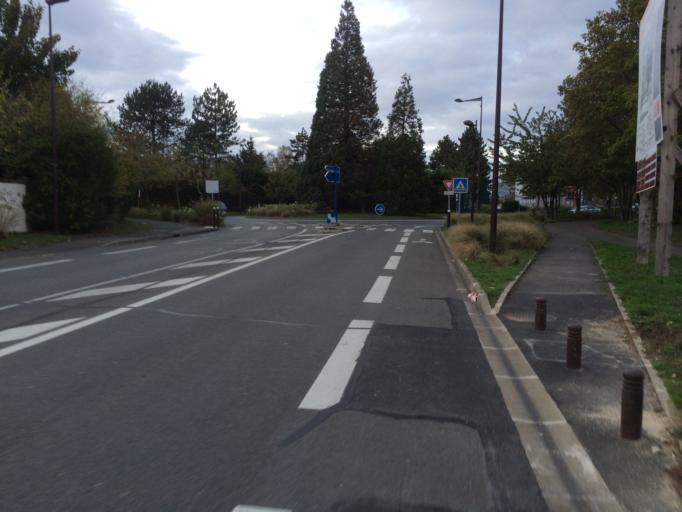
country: FR
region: Ile-de-France
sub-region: Departement de l'Essonne
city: Les Ulis
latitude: 48.6787
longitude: 2.1627
